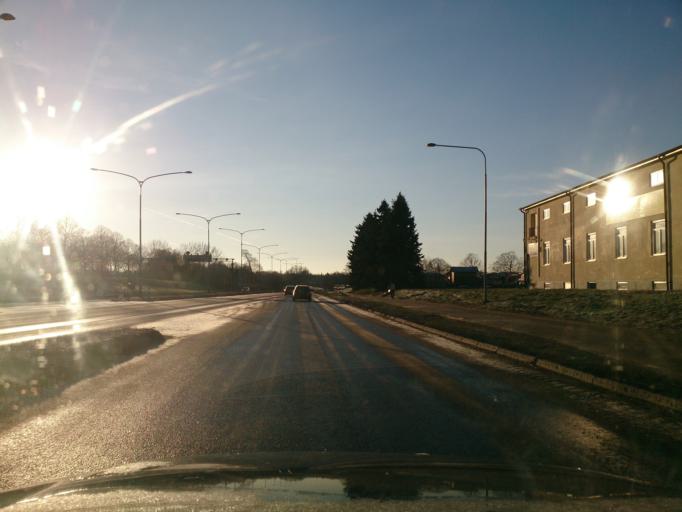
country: SE
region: OEstergoetland
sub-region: Norrkopings Kommun
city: Norrkoping
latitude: 58.5938
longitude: 16.1568
